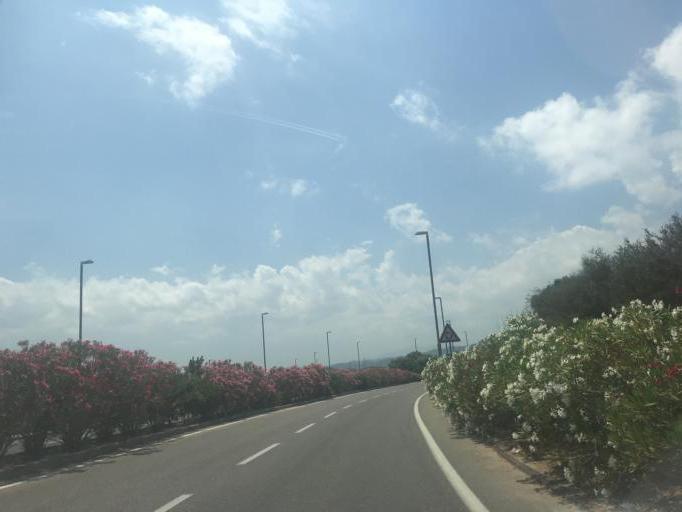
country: IT
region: Sardinia
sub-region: Provincia di Olbia-Tempio
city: Olbia
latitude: 40.9021
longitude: 9.5097
